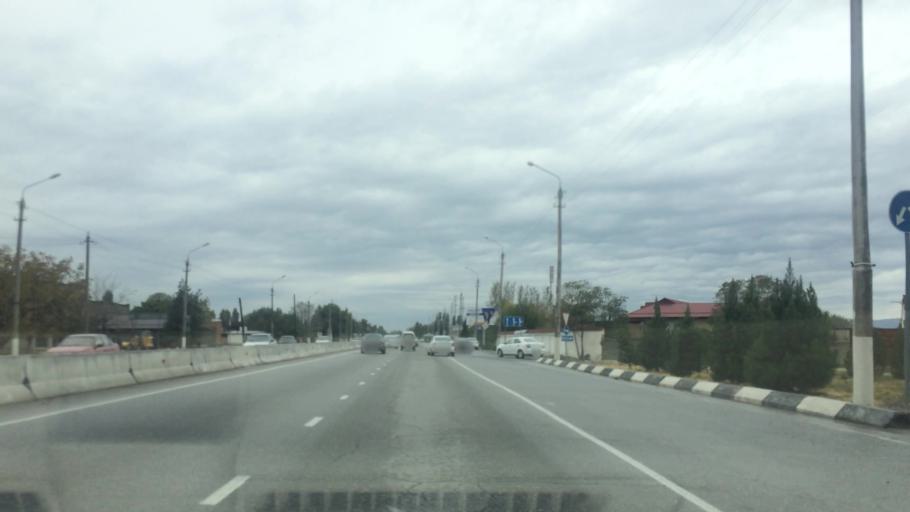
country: UZ
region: Jizzax
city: Jizzax
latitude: 40.0045
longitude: 67.5946
